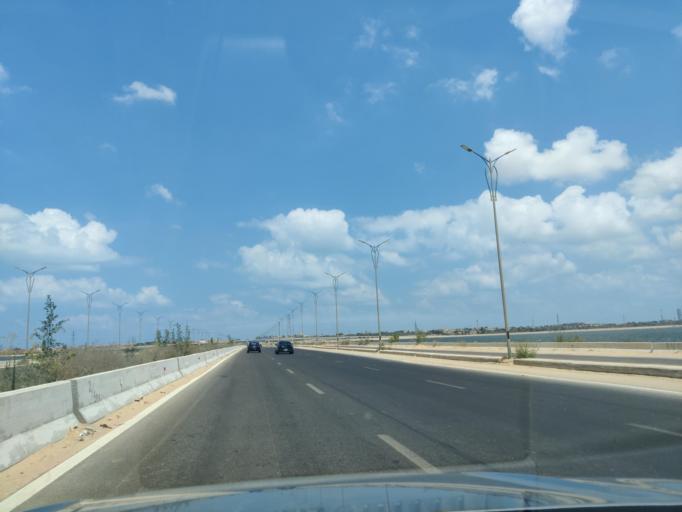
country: EG
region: Alexandria
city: Alexandria
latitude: 30.9941
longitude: 29.6479
